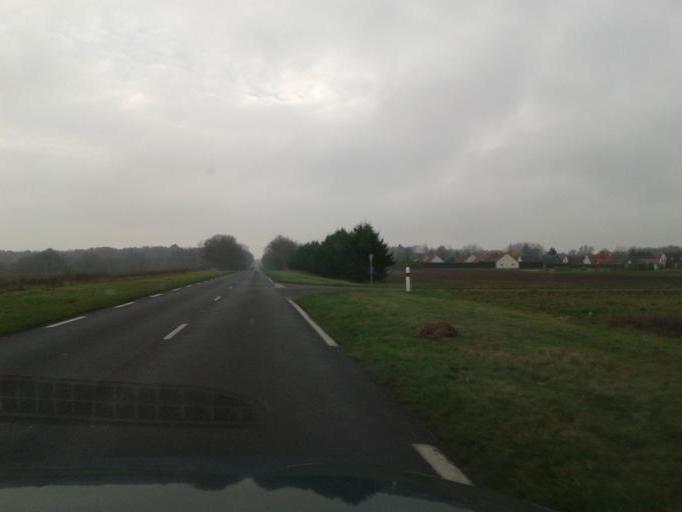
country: FR
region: Centre
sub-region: Departement du Loiret
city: Lailly-en-Val
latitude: 47.7426
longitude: 1.6567
